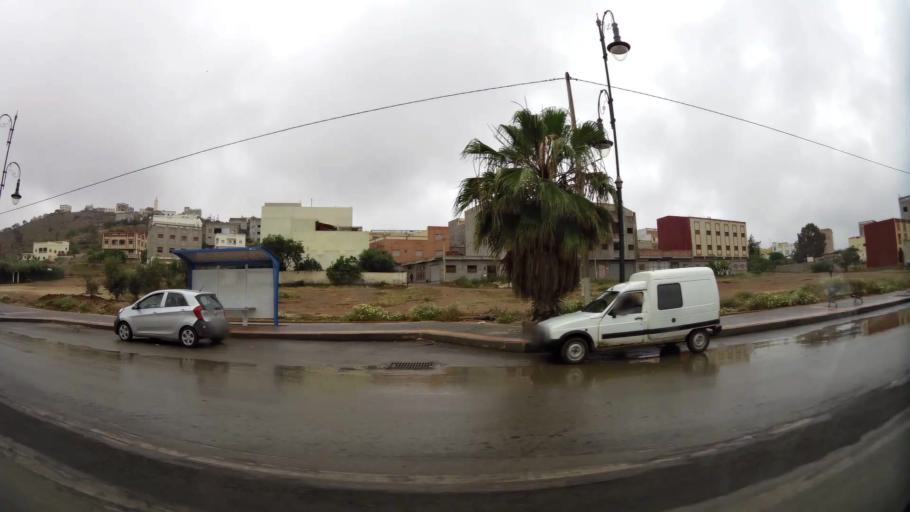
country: MA
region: Taza-Al Hoceima-Taounate
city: Imzourene
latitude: 35.1724
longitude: -3.8637
